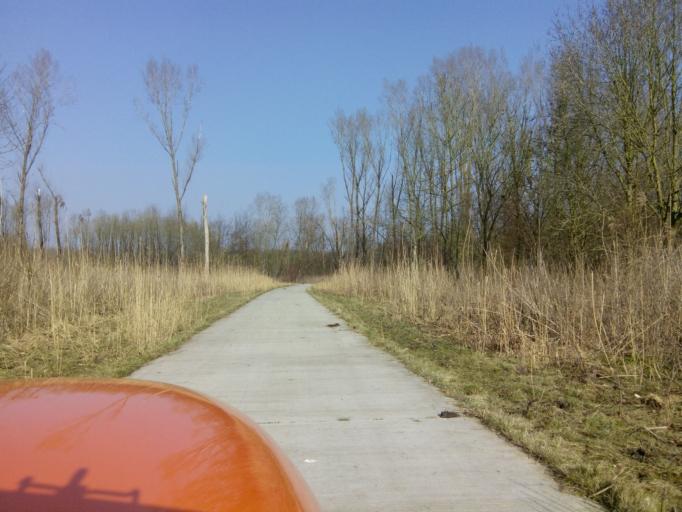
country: NL
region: Gelderland
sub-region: Gemeente Nijkerk
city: Nijkerk
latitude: 52.2838
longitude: 5.4642
